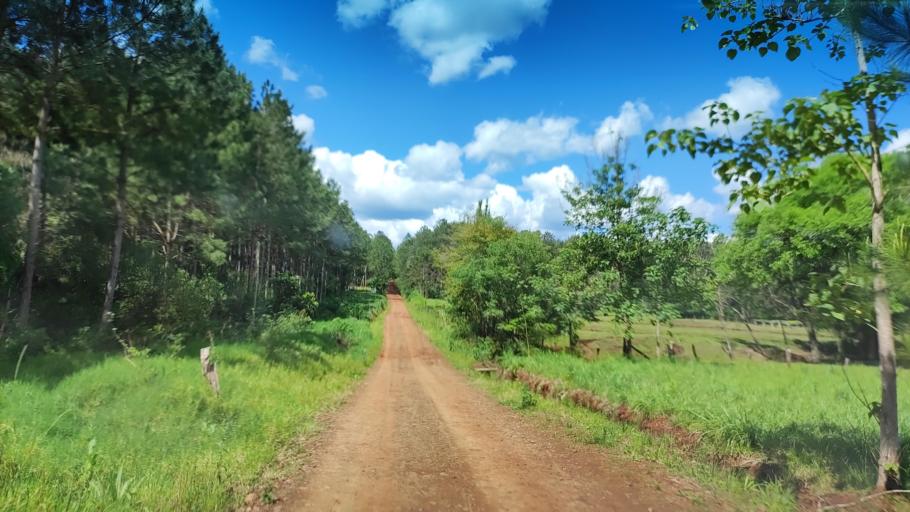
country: AR
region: Misiones
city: Ruiz de Montoya
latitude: -26.9528
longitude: -55.0105
